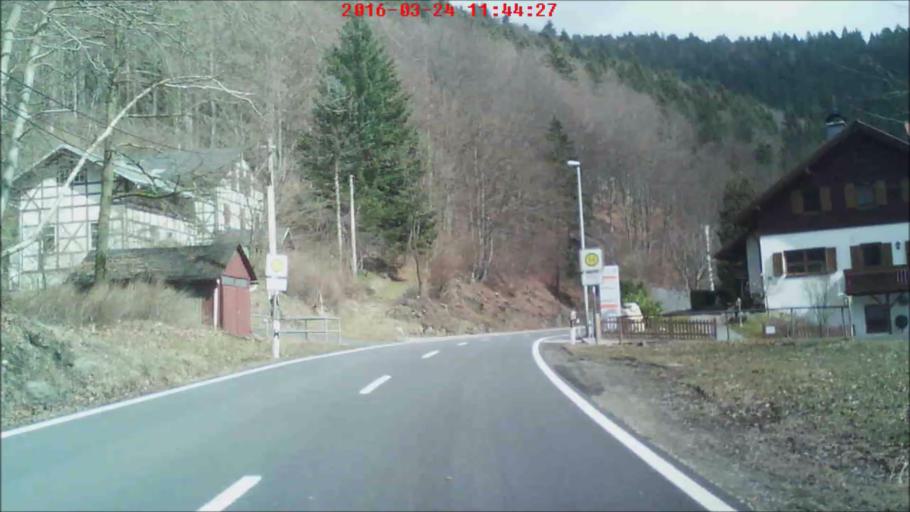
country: DE
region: Thuringia
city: Bachfeld
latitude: 50.4558
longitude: 10.9808
